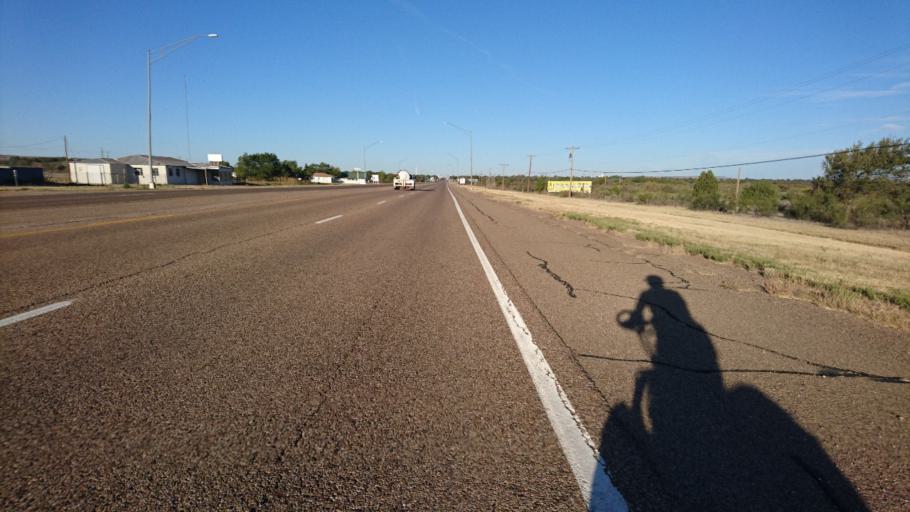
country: US
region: New Mexico
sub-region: Quay County
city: Tucumcari
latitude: 35.1719
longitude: -103.6904
